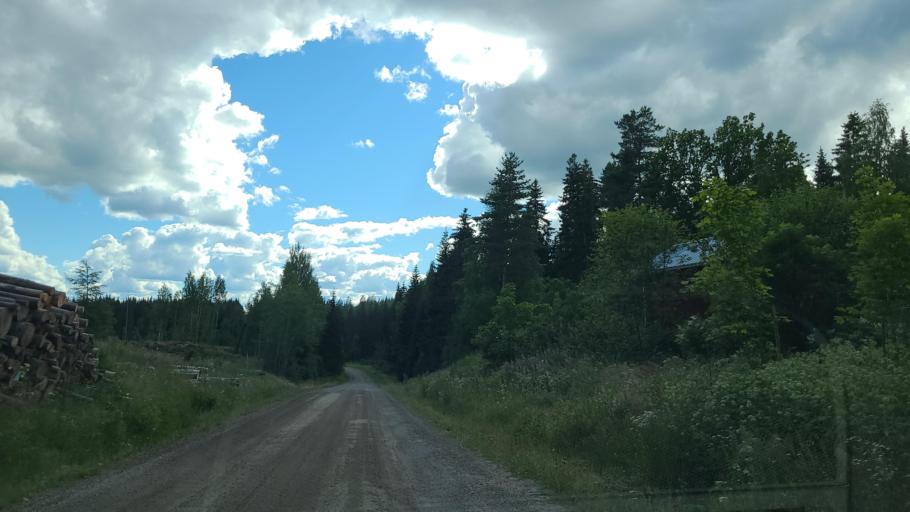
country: FI
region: Central Finland
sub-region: Jaemsae
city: Jaemsae
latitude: 61.9244
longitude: 25.3153
